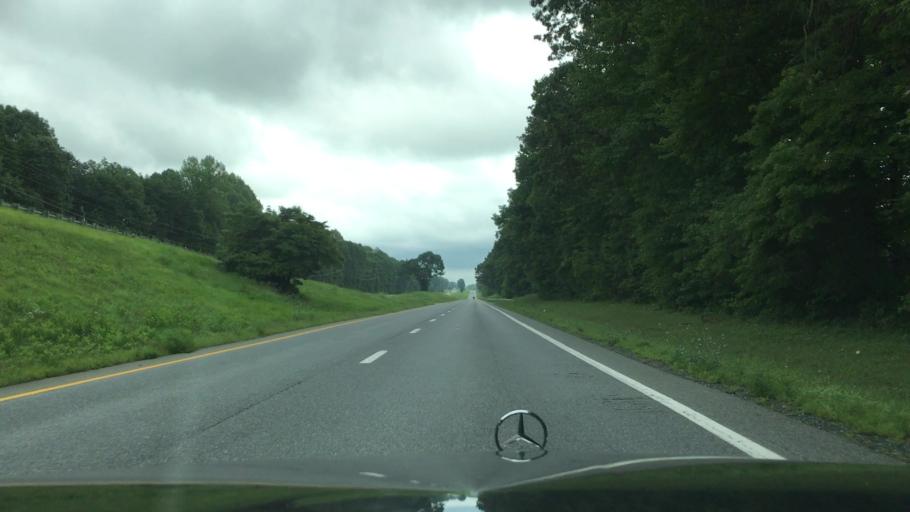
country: US
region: Virginia
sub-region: Appomattox County
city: Appomattox
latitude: 37.2846
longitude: -78.7167
